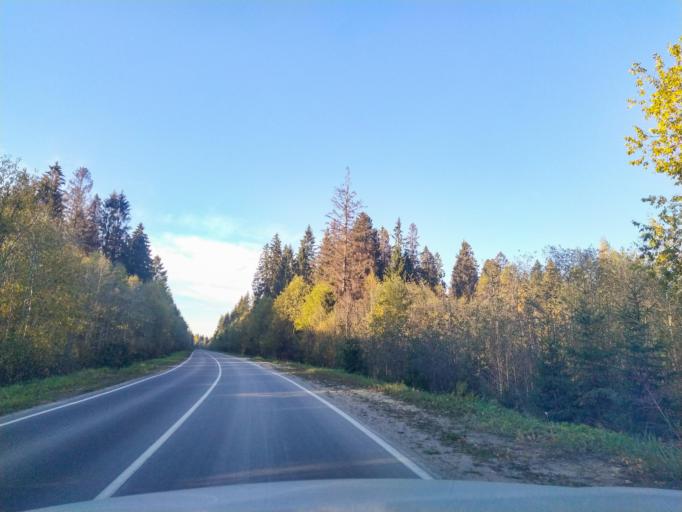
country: RU
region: Leningrad
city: Siverskiy
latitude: 59.3030
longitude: 30.0353
